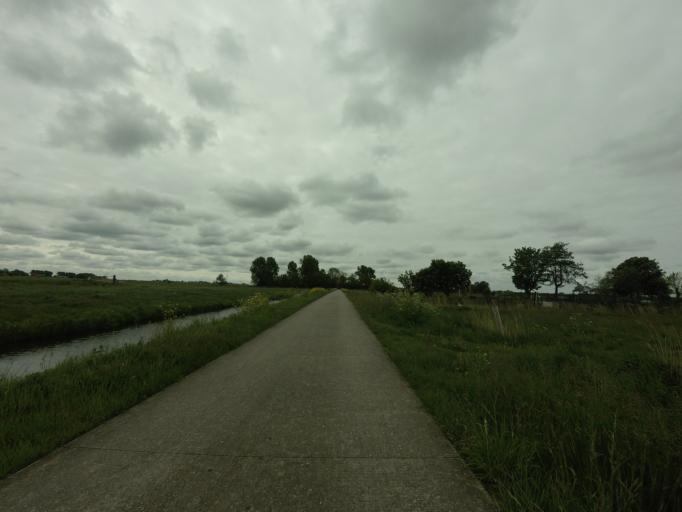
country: NL
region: Friesland
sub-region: Sudwest Fryslan
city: Workum
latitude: 52.9998
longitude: 5.4638
